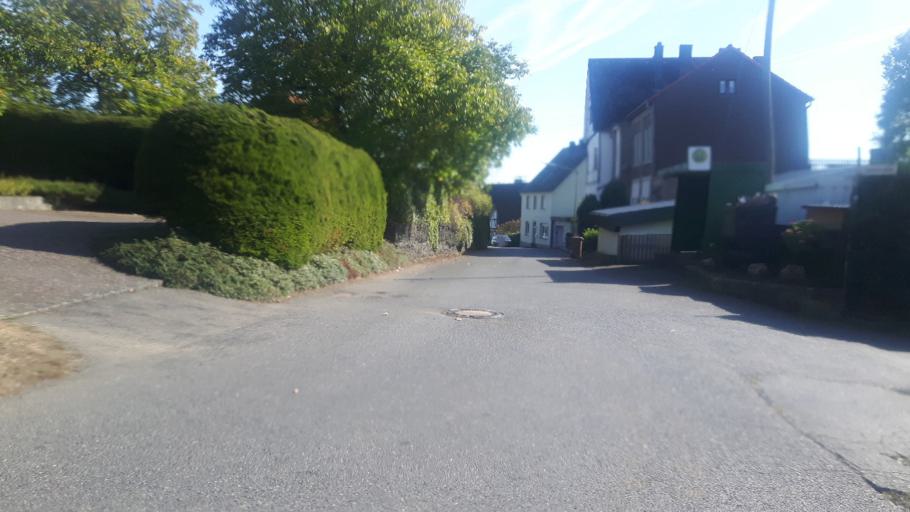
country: DE
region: Rheinland-Pfalz
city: Etzbach
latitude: 50.7868
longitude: 7.6943
